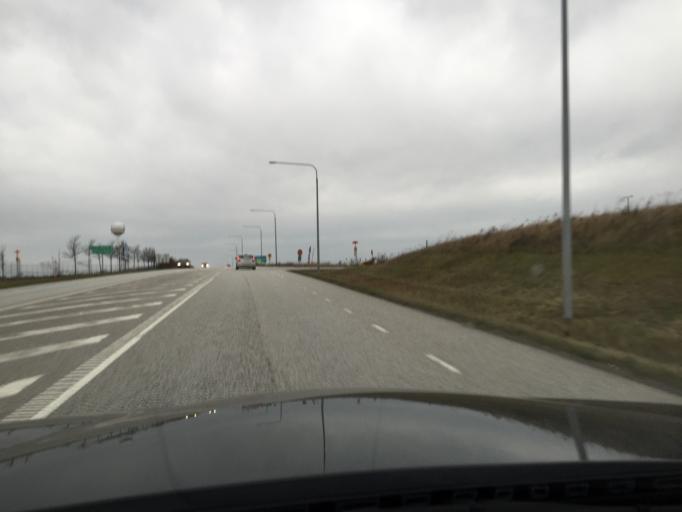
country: SE
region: Skane
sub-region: Malmo
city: Oxie
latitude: 55.5880
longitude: 13.1185
